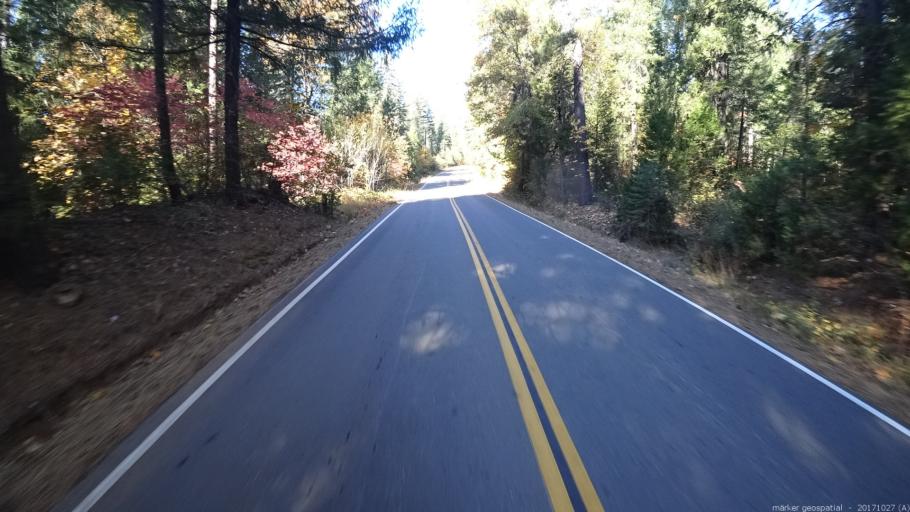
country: US
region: California
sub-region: Shasta County
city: Burney
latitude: 40.9242
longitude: -121.9135
